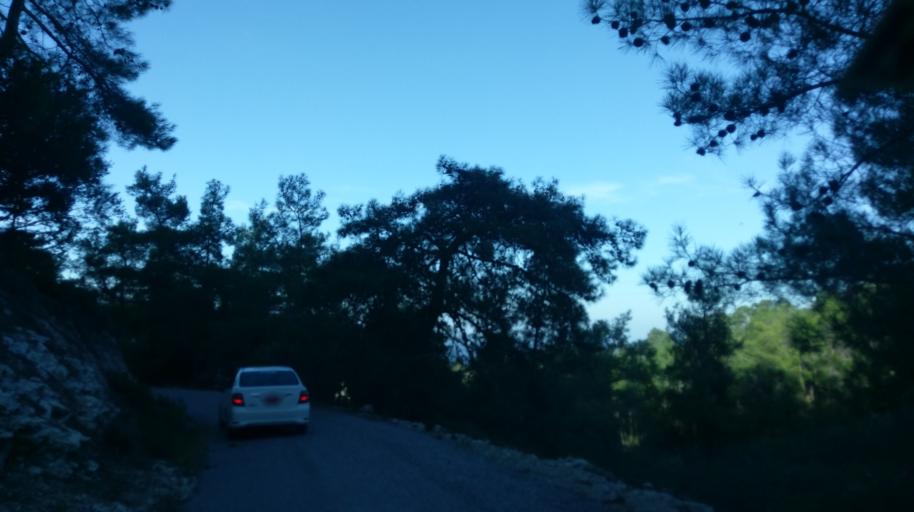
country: CY
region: Ammochostos
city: Lefkonoiko
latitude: 35.3239
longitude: 33.6120
